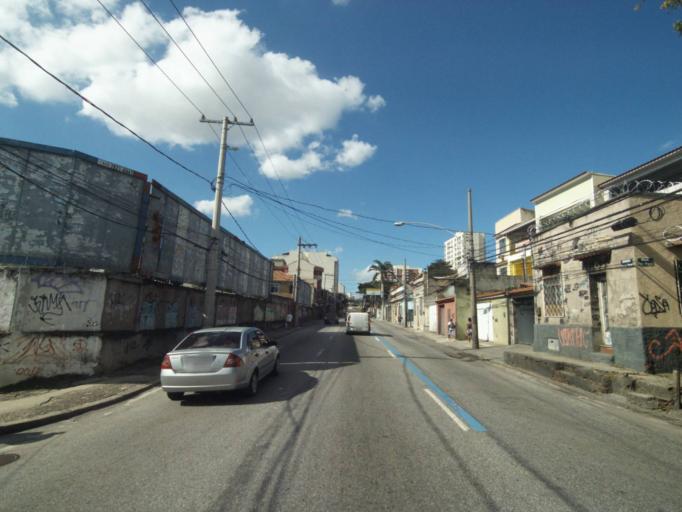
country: BR
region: Rio de Janeiro
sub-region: Rio De Janeiro
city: Rio de Janeiro
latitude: -22.9031
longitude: -43.2525
